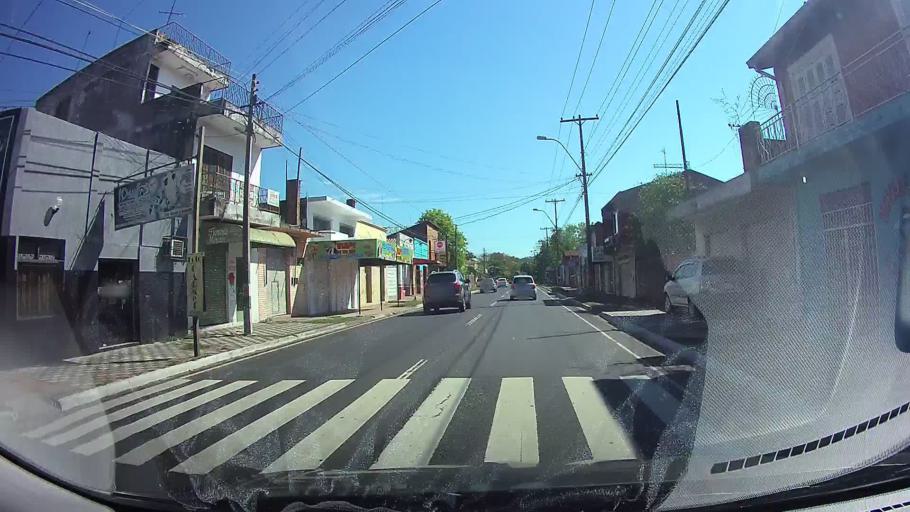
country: PY
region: Central
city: Ypacarai
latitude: -25.4002
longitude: -57.2874
